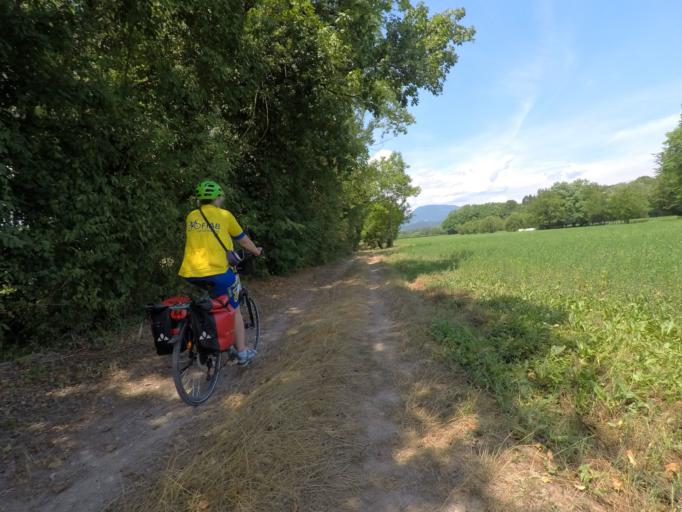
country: IT
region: Friuli Venezia Giulia
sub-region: Provincia di Pordenone
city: Lestans
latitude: 46.1463
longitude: 12.9079
